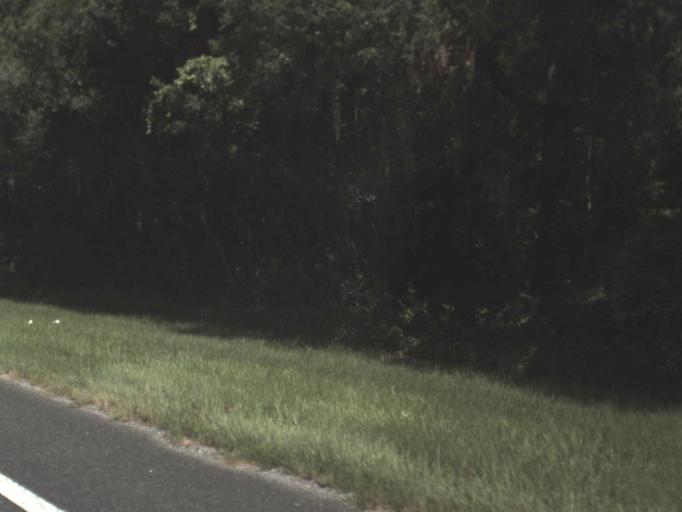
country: US
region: Florida
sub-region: Levy County
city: Manatee Road
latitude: 29.6023
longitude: -82.9980
